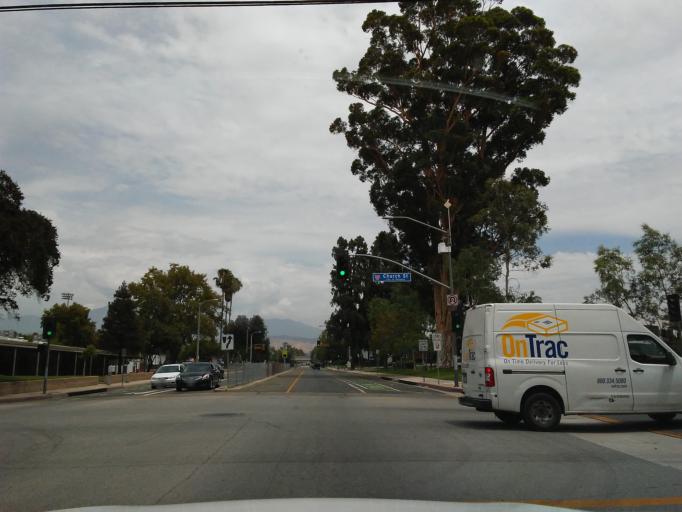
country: US
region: California
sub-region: San Bernardino County
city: Redlands
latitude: 34.0555
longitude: -117.1741
